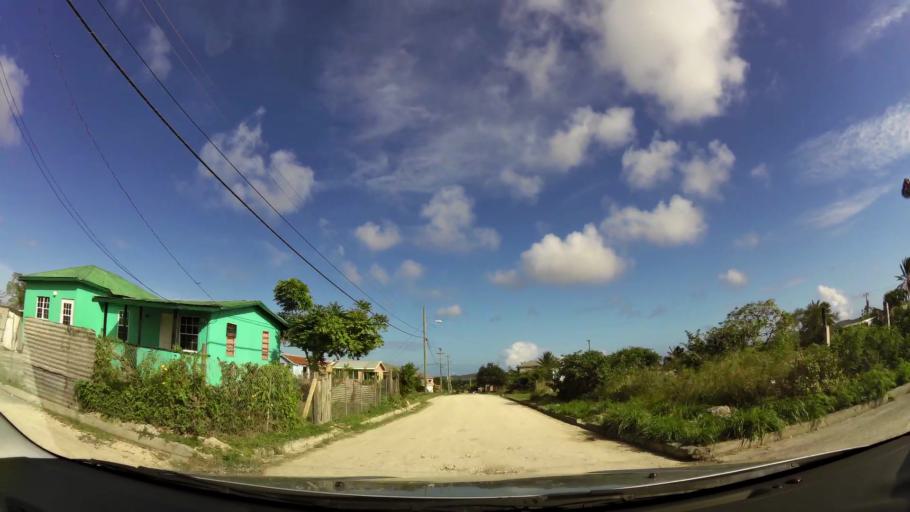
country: AG
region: Saint Peter
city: All Saints
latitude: 17.0672
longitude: -61.7890
